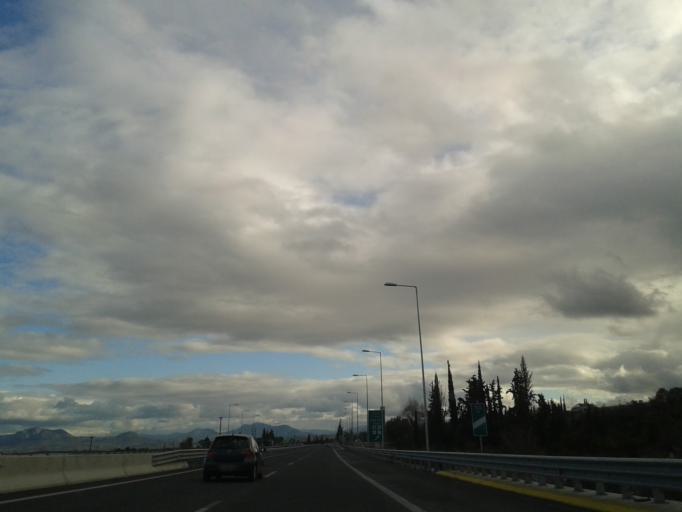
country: GR
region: Peloponnese
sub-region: Nomos Korinthias
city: Sikyon
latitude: 37.9784
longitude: 22.7383
